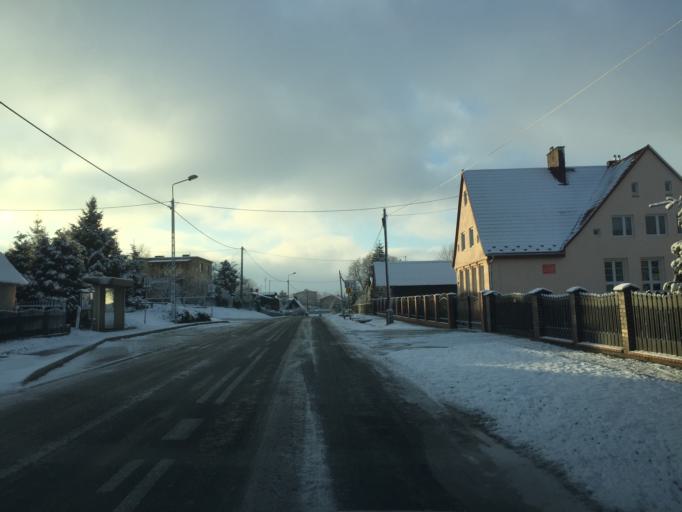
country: PL
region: Kujawsko-Pomorskie
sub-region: Powiat brodnicki
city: Bartniczka
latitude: 53.2482
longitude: 19.5495
